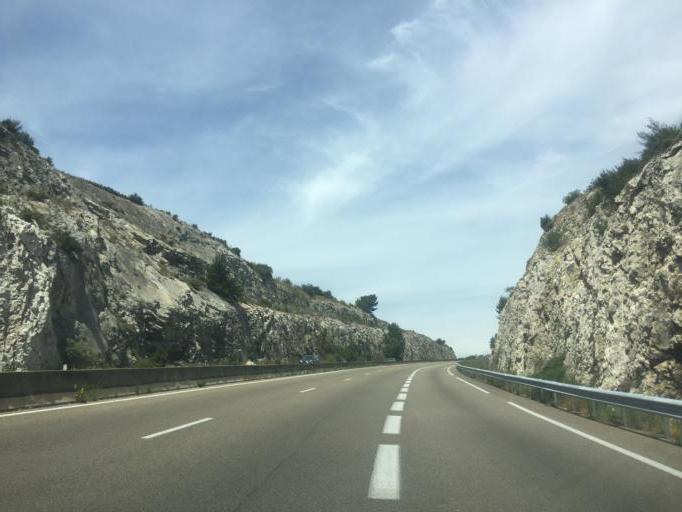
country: FR
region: Languedoc-Roussillon
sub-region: Departement du Gard
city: Les Angles
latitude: 43.9516
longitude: 4.7587
